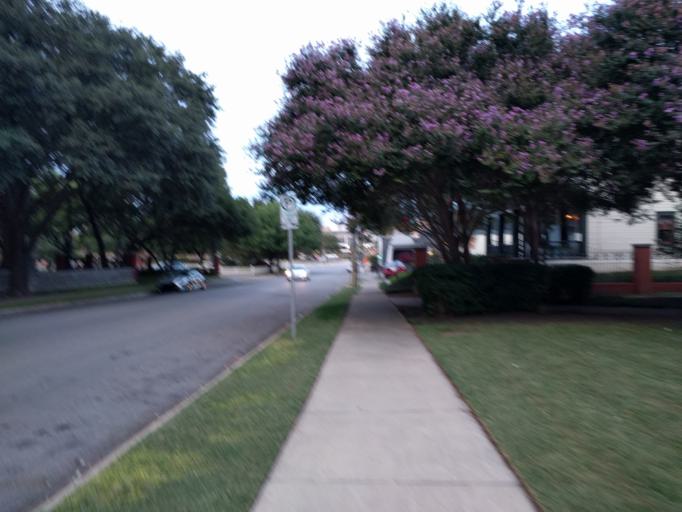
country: US
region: Texas
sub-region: Dallas County
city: Dallas
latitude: 32.7894
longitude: -96.7845
